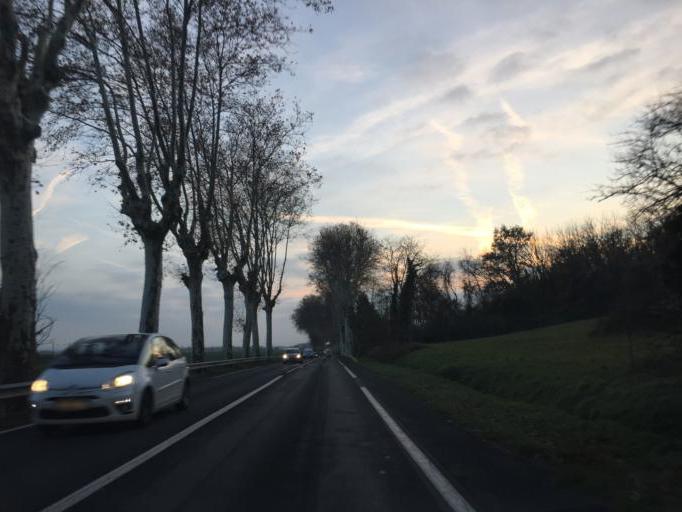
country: FR
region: Rhone-Alpes
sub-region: Departement de l'Ain
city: Perouges
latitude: 45.8969
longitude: 5.1838
